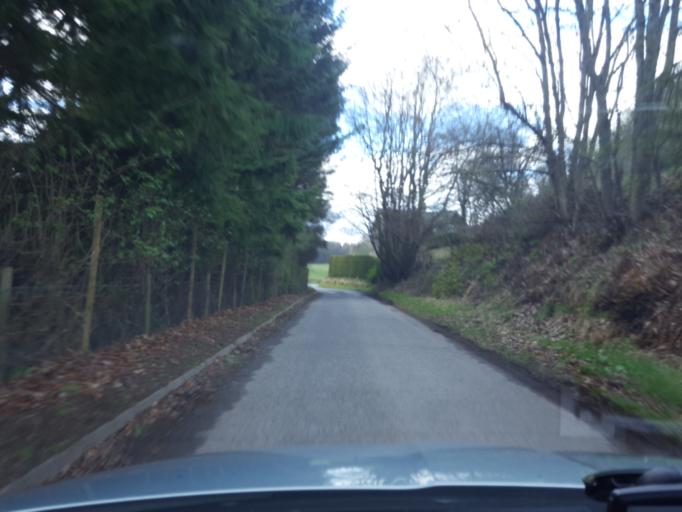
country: GB
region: Scotland
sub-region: Perth and Kinross
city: Scone
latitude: 56.3928
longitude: -3.3801
